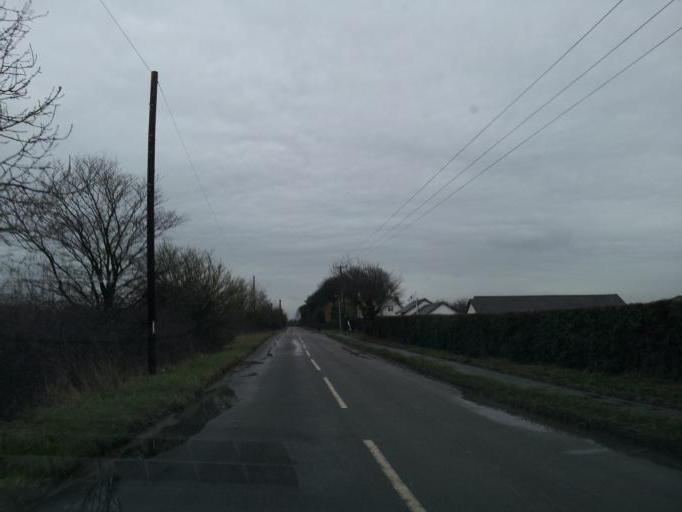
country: GB
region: England
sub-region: Cambridgeshire
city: Bottisham
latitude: 52.2346
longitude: 0.2490
